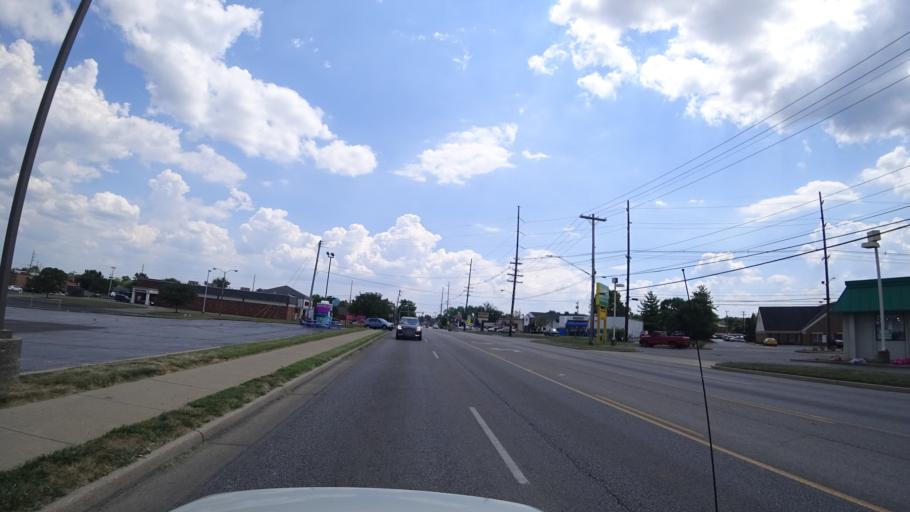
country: US
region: Ohio
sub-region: Butler County
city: Hamilton
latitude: 39.4211
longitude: -84.5907
